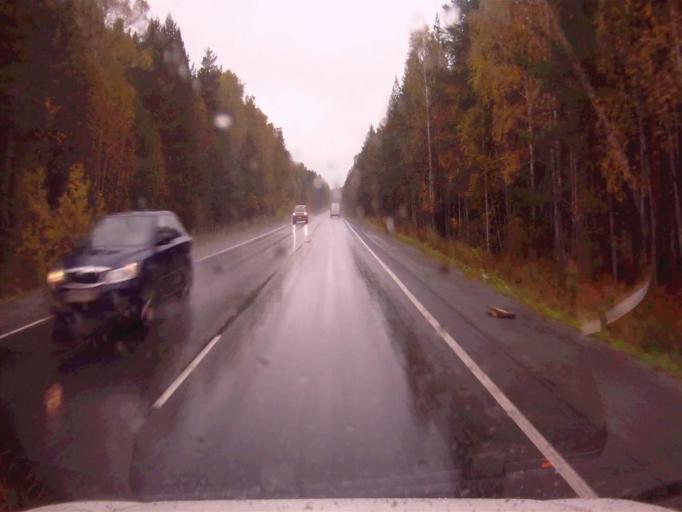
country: RU
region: Chelyabinsk
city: Tayginka
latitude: 55.5602
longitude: 60.6473
